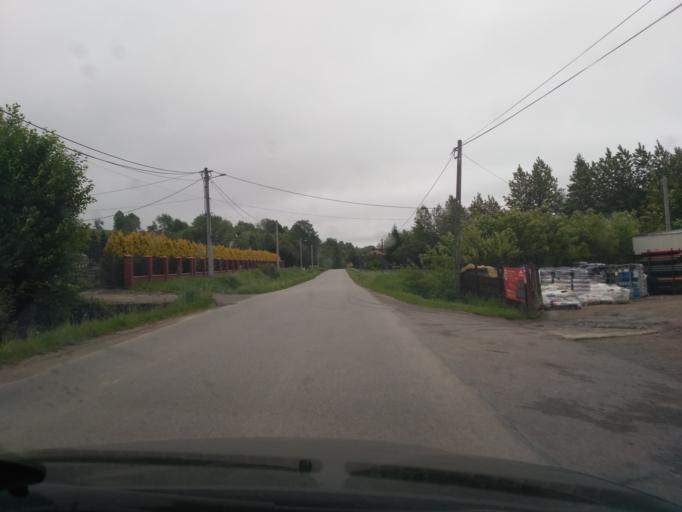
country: PL
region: Subcarpathian Voivodeship
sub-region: Powiat debicki
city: Jodlowa
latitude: 49.8719
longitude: 21.2467
